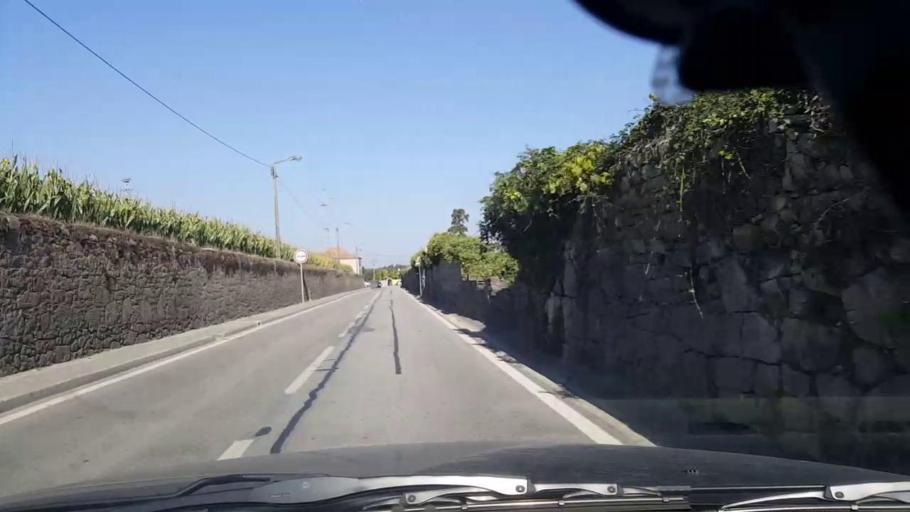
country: PT
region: Porto
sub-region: Vila do Conde
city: Arvore
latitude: 41.3789
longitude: -8.6783
